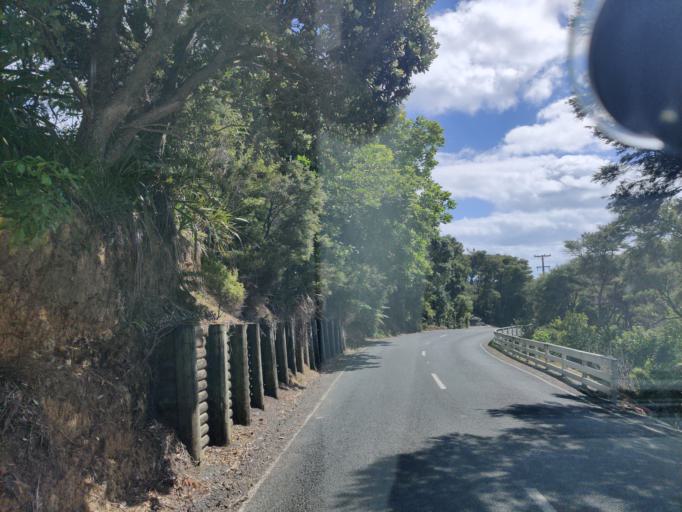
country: NZ
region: Northland
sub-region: Far North District
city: Paihia
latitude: -35.2584
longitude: 174.2447
